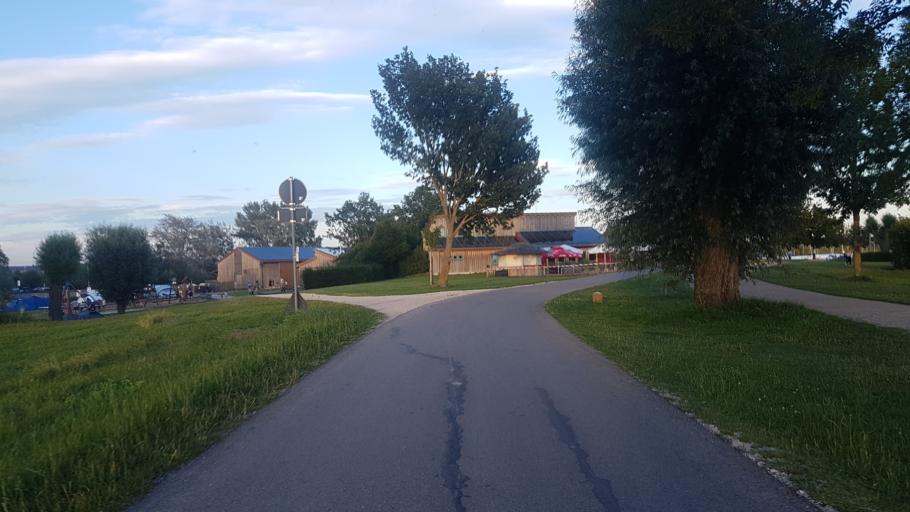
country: DE
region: Bavaria
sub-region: Regierungsbezirk Mittelfranken
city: Muhr am See
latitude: 49.1450
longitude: 10.7240
